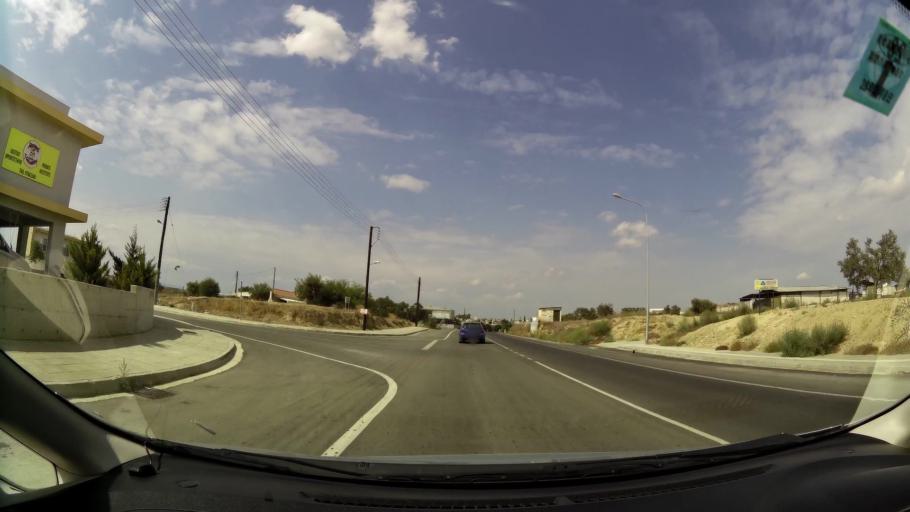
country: CY
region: Lefkosia
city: Tseri
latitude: 35.0667
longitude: 33.3348
